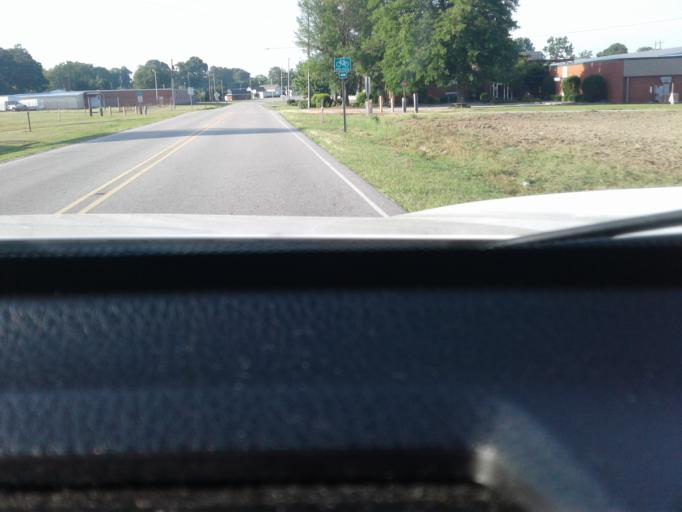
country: US
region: North Carolina
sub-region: Harnett County
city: Dunn
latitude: 35.3199
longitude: -78.6212
